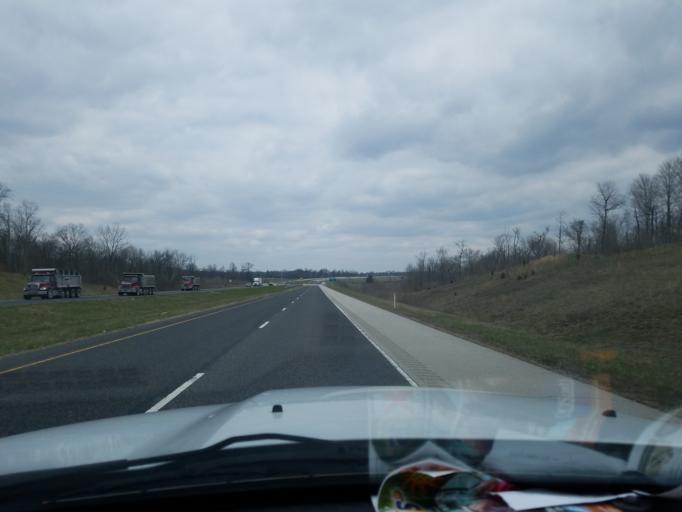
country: US
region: Indiana
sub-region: Vigo County
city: Terre Haute
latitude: 39.3881
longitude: -87.3729
